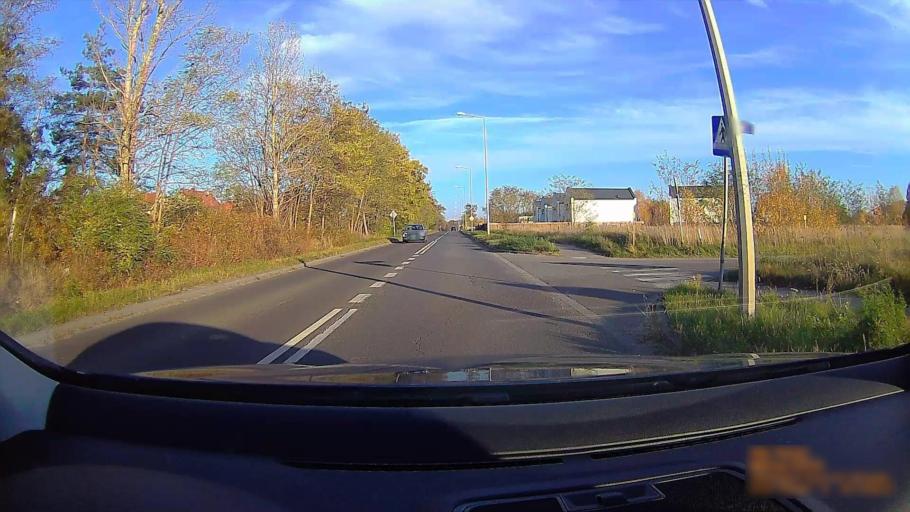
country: PL
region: Greater Poland Voivodeship
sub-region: Powiat koninski
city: Stare Miasto
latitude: 52.2026
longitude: 18.2117
